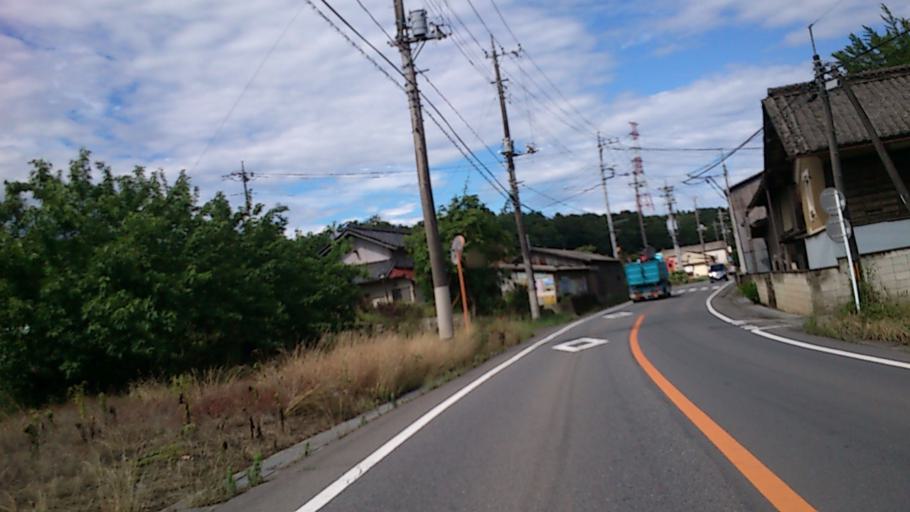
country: JP
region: Gunma
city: Fujioka
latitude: 36.2570
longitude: 139.0291
